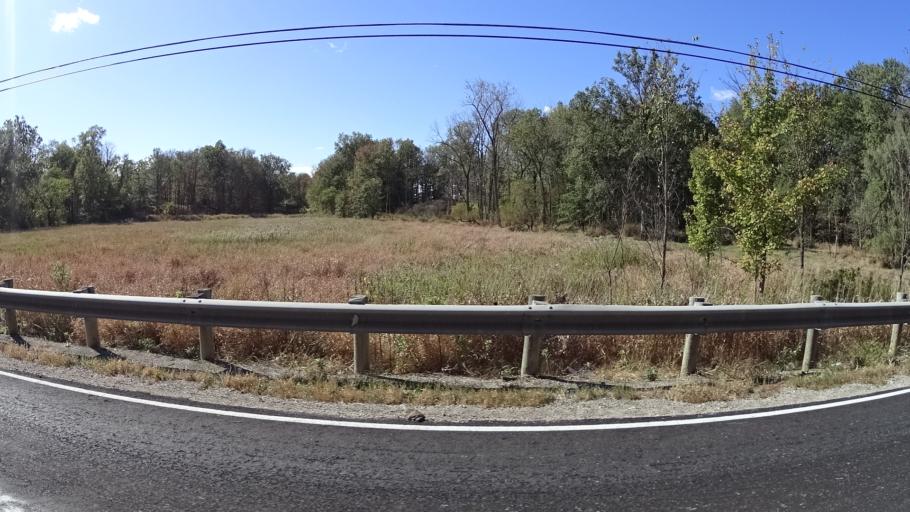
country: US
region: Ohio
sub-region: Lorain County
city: Grafton
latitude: 41.3095
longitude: -82.0892
